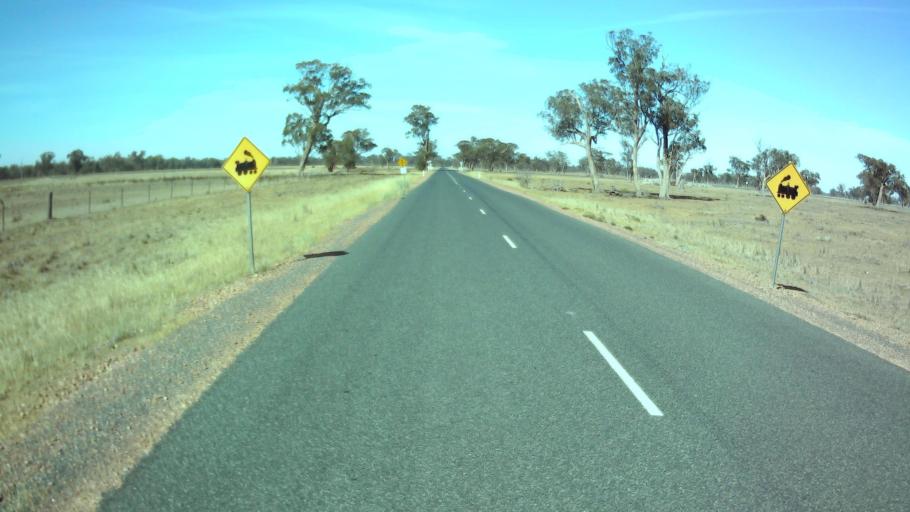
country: AU
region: New South Wales
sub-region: Weddin
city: Grenfell
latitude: -34.1055
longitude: 147.8648
